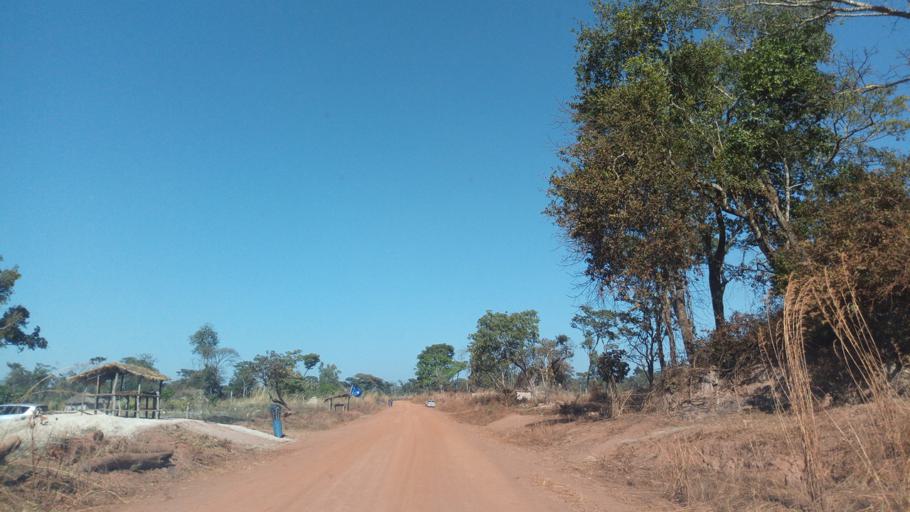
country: ZM
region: Luapula
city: Mwense
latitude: -10.7024
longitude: 28.3780
